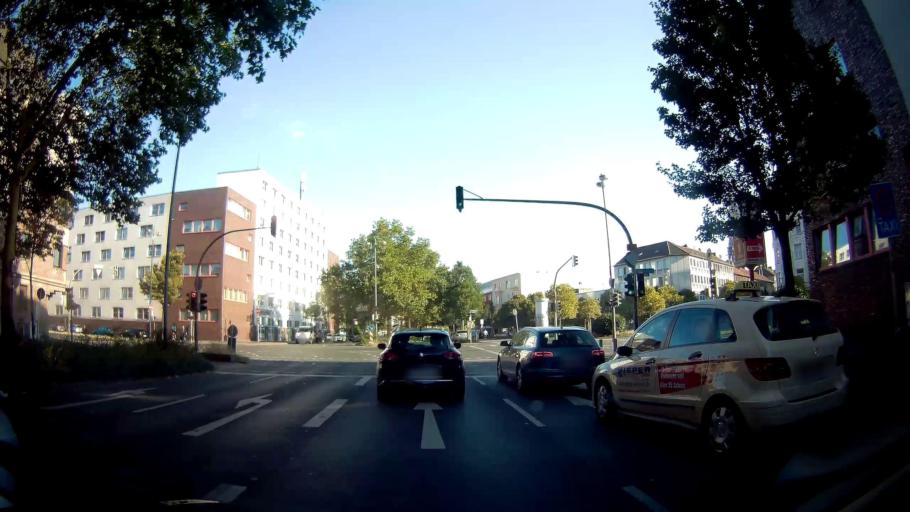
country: DE
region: North Rhine-Westphalia
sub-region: Regierungsbezirk Arnsberg
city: Dortmund
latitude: 51.5241
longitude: 7.4612
